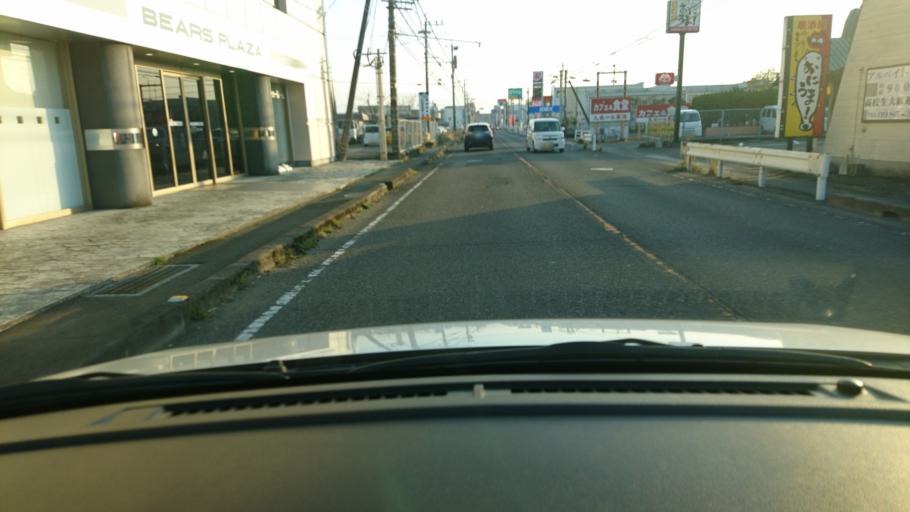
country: JP
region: Miyazaki
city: Miyazaki-shi
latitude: 31.9568
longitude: 131.4360
